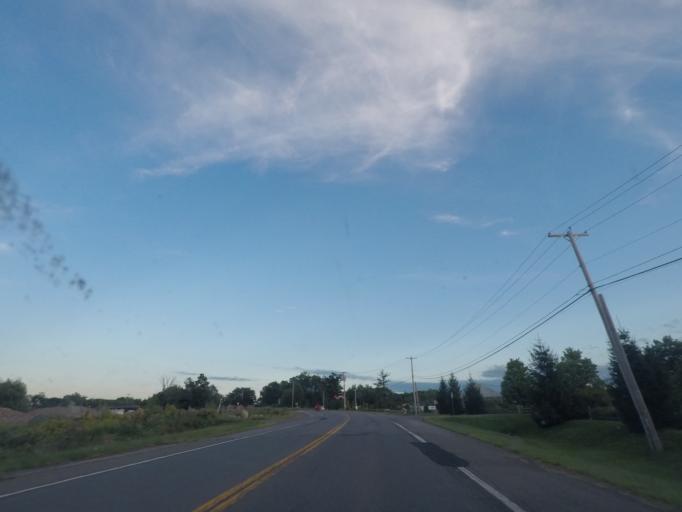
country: US
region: New York
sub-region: Albany County
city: Cohoes
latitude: 42.7611
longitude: -73.7675
